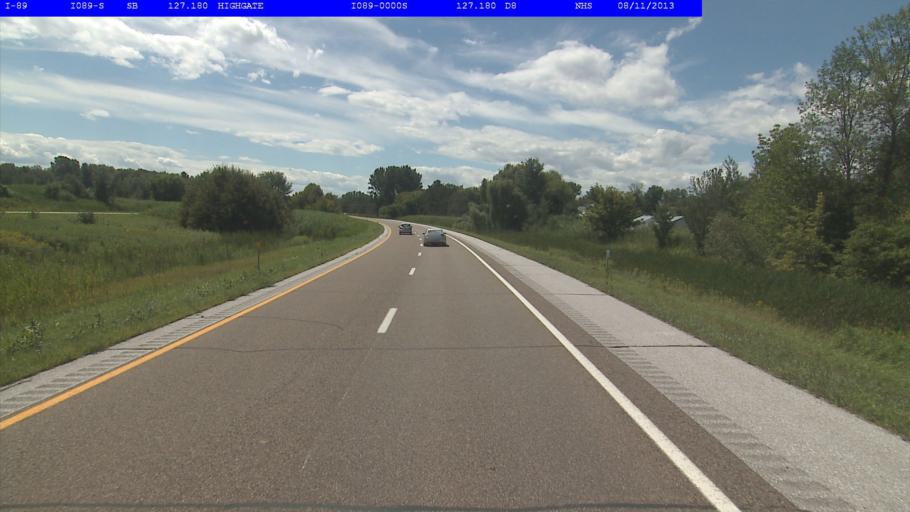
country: US
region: Vermont
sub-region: Franklin County
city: Swanton
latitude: 44.9757
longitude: -73.1029
